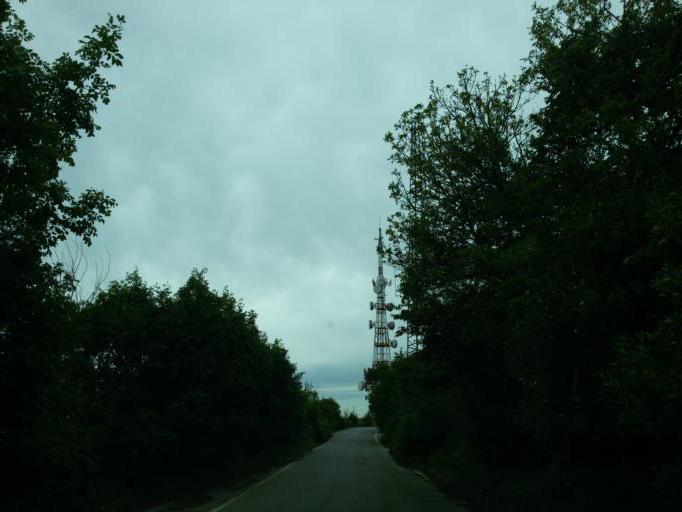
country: IT
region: Liguria
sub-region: Provincia di Genova
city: Genoa
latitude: 44.4322
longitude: 8.9137
